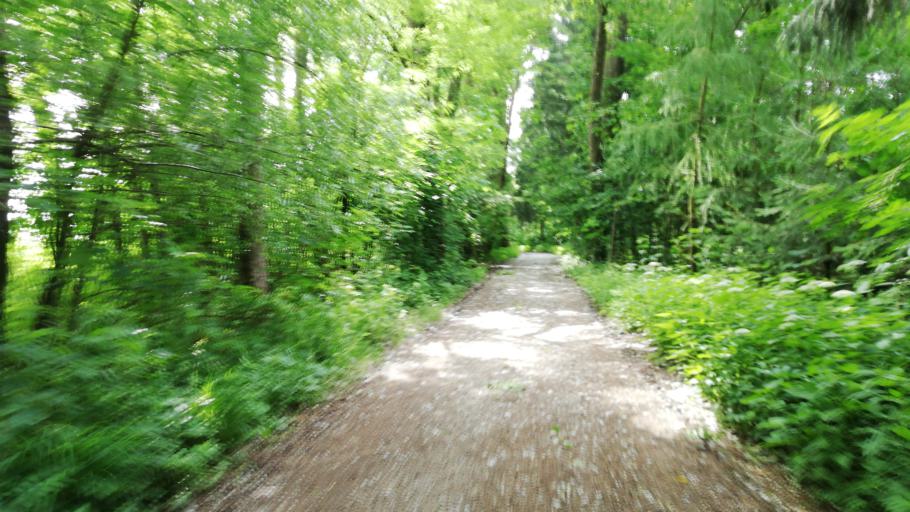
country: AT
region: Upper Austria
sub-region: Politischer Bezirk Grieskirchen
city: Bad Schallerbach
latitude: 48.2418
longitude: 13.9260
